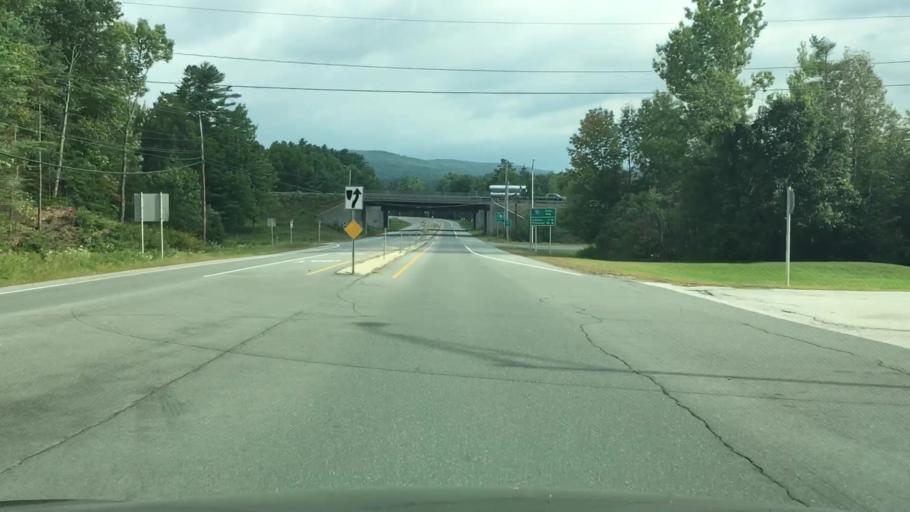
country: US
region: New Hampshire
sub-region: Grafton County
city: Littleton
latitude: 44.3274
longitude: -71.8747
